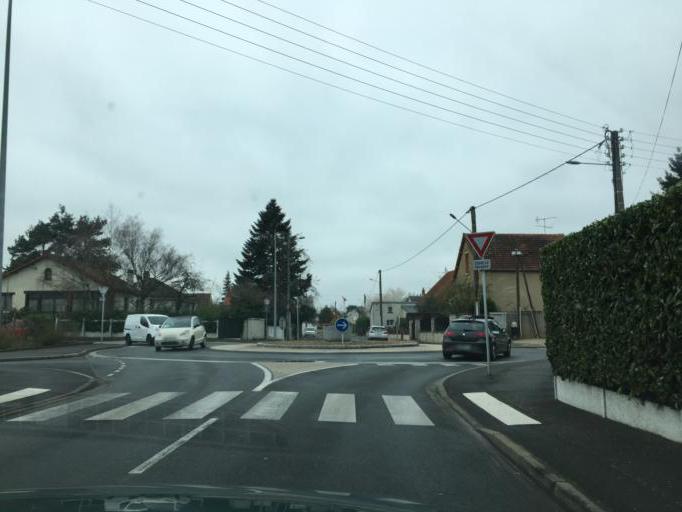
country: FR
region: Centre
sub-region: Departement du Loiret
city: Saint-Jean-le-Blanc
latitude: 47.8822
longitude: 1.9188
